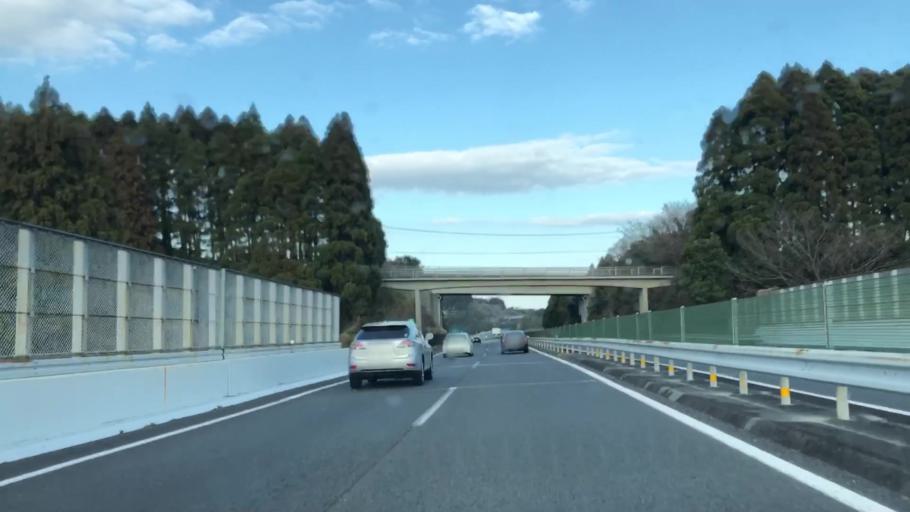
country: JP
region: Miyazaki
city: Miyazaki-shi
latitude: 31.8574
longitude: 131.3759
